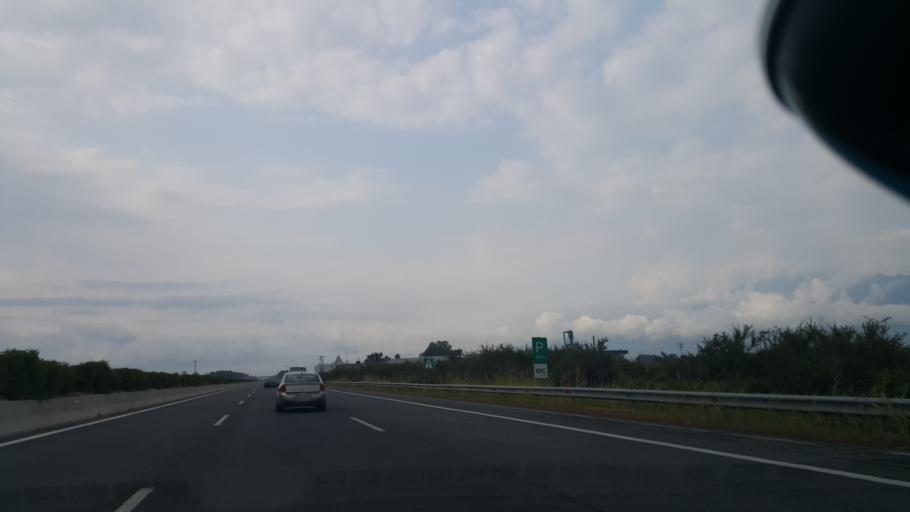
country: GR
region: Central Macedonia
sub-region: Nomos Pierias
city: Peristasi
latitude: 40.2414
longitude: 22.5356
